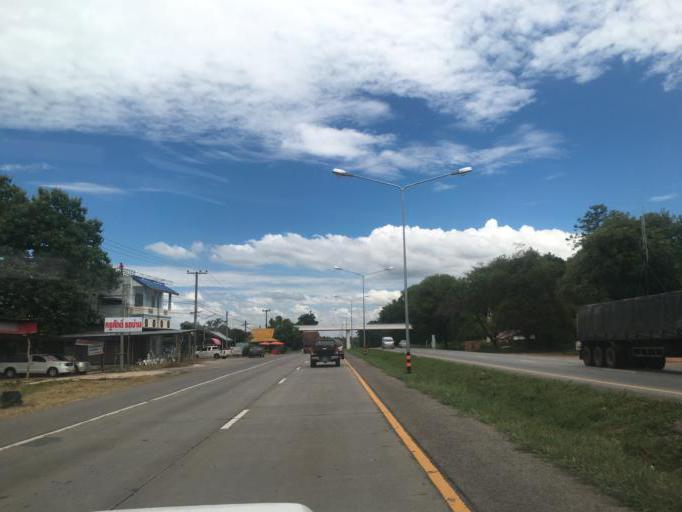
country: TH
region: Khon Kaen
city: Nam Phong
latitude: 16.6328
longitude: 102.7995
